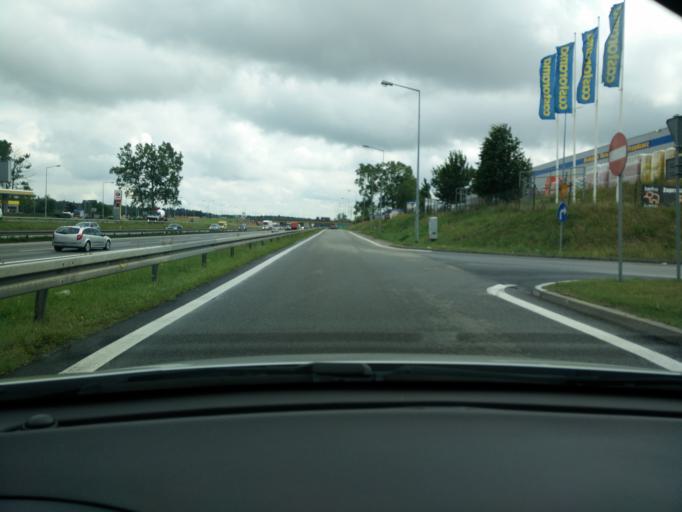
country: PL
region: Pomeranian Voivodeship
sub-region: Gdynia
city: Wielki Kack
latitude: 54.4336
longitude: 18.4874
